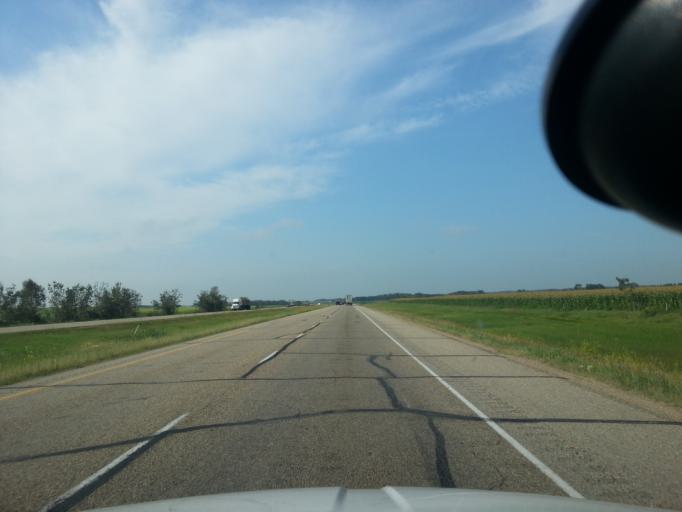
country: CA
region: Alberta
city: Blackfalds
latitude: 52.4395
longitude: -113.8091
